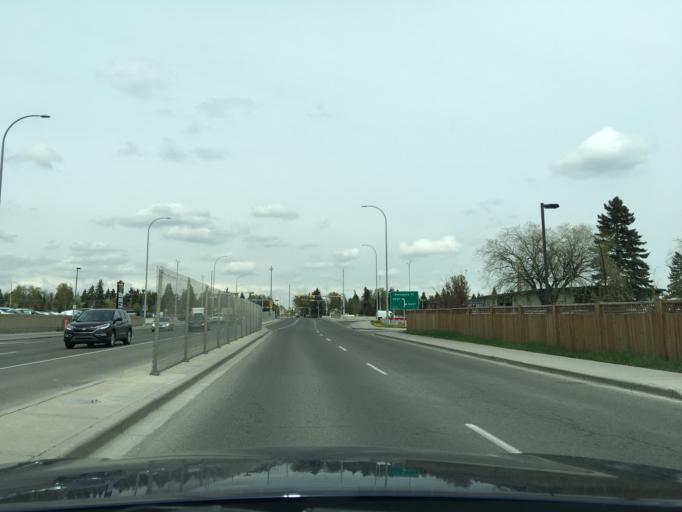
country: CA
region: Alberta
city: Calgary
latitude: 50.9928
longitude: -114.0831
